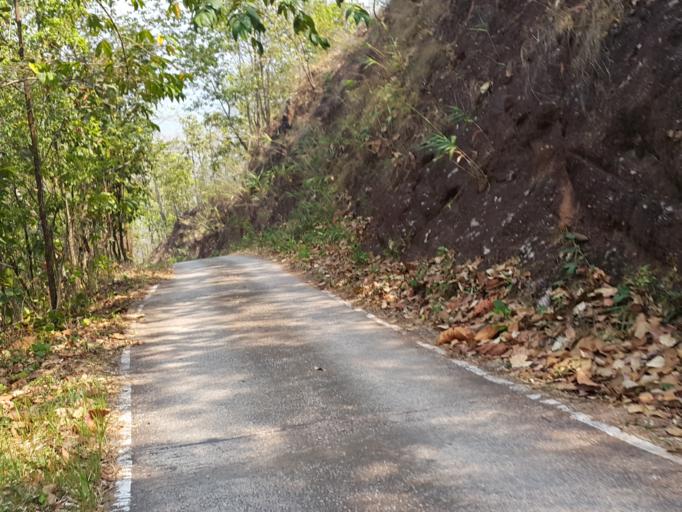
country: TH
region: Lampang
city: Mueang Pan
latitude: 18.7514
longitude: 99.5338
